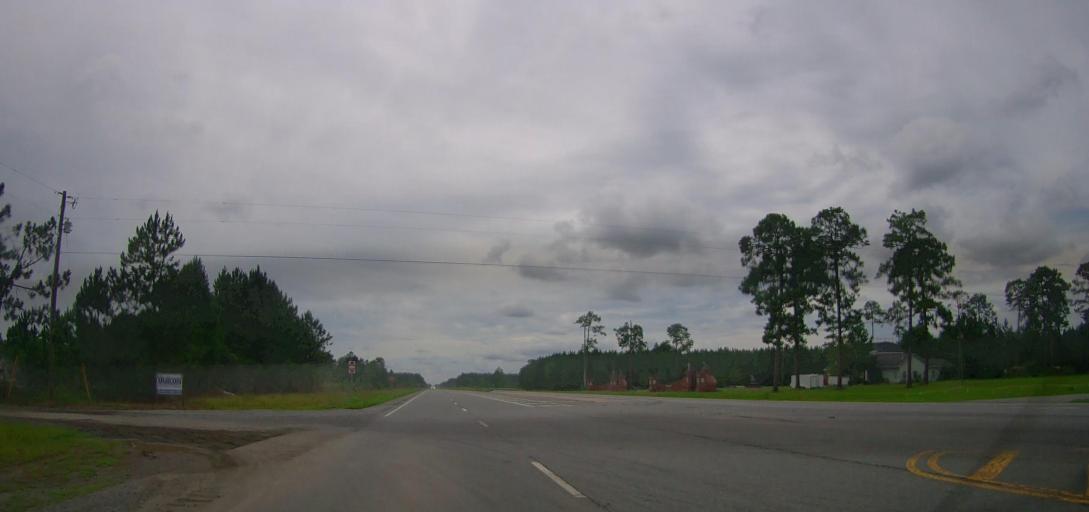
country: US
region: Georgia
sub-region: Appling County
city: Baxley
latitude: 31.7375
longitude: -82.2313
